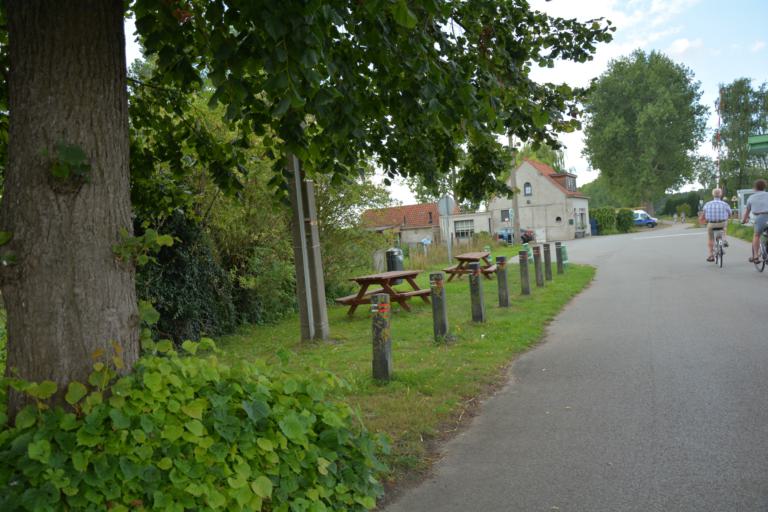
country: BE
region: Flanders
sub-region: Provincie Oost-Vlaanderen
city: Moerbeke
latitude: 51.1704
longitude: 3.9182
